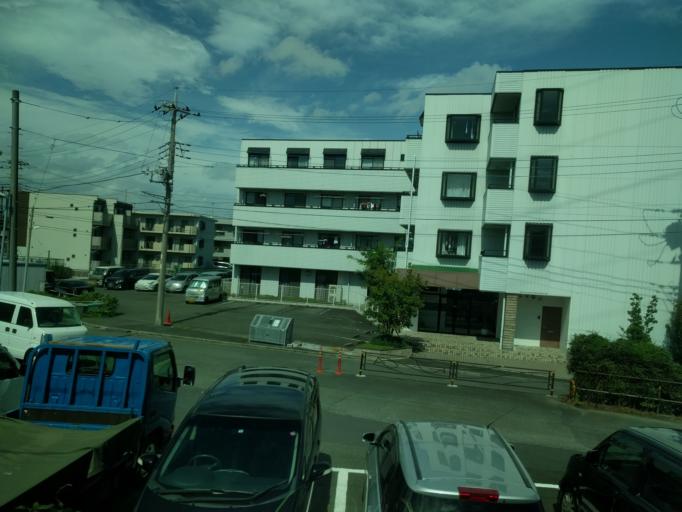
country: JP
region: Tokyo
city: Chofugaoka
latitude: 35.6141
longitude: 139.5850
